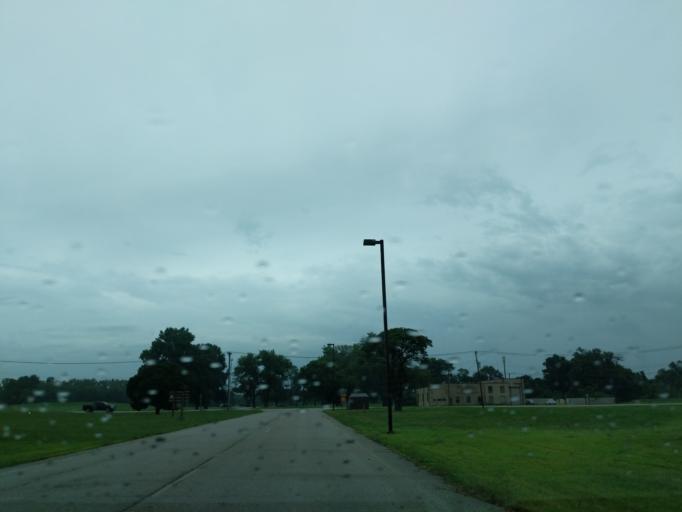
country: US
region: Illinois
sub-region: Saint Clair County
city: Fairmont City
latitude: 38.6575
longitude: -90.0587
